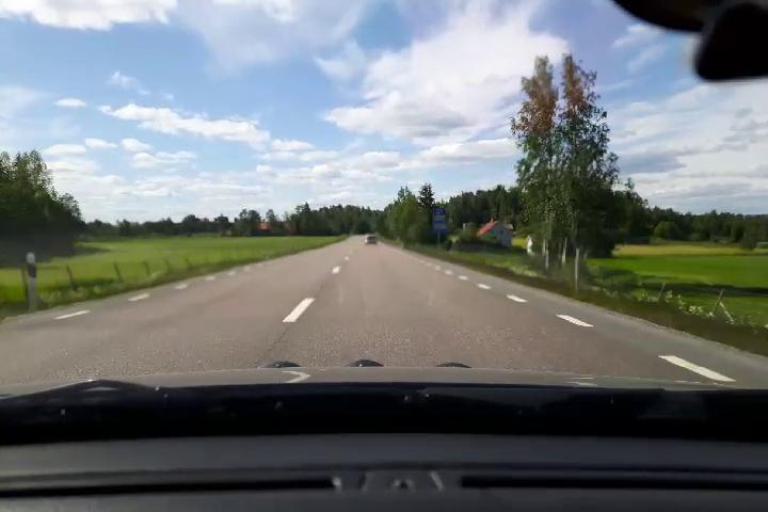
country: SE
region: Gaevleborg
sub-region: Bollnas Kommun
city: Bollnas
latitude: 61.3097
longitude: 16.4525
